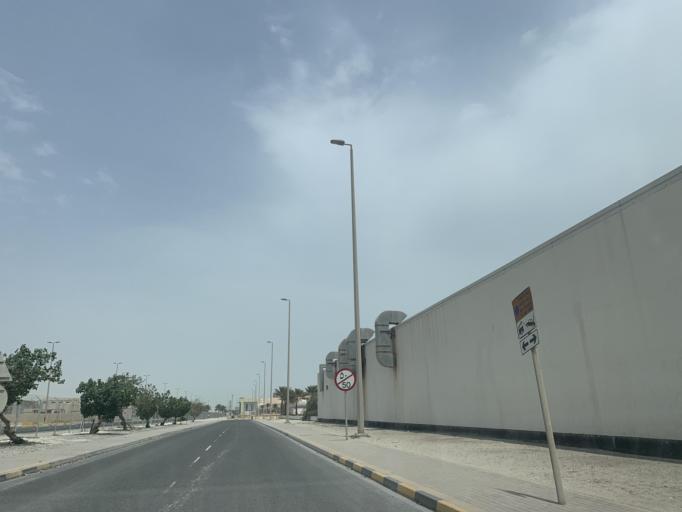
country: BH
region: Muharraq
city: Al Hadd
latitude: 26.2167
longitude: 50.6676
